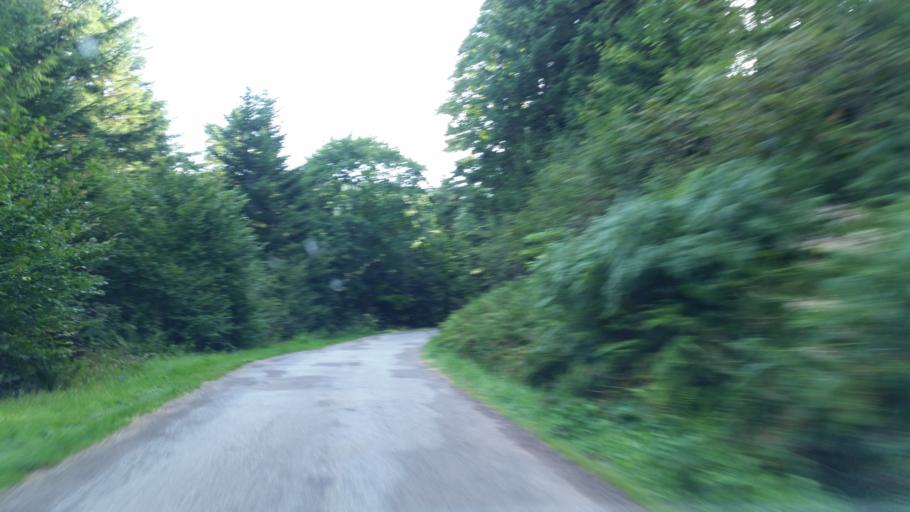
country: FR
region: Lorraine
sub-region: Departement des Vosges
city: Remiremont
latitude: 47.9566
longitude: 6.5553
